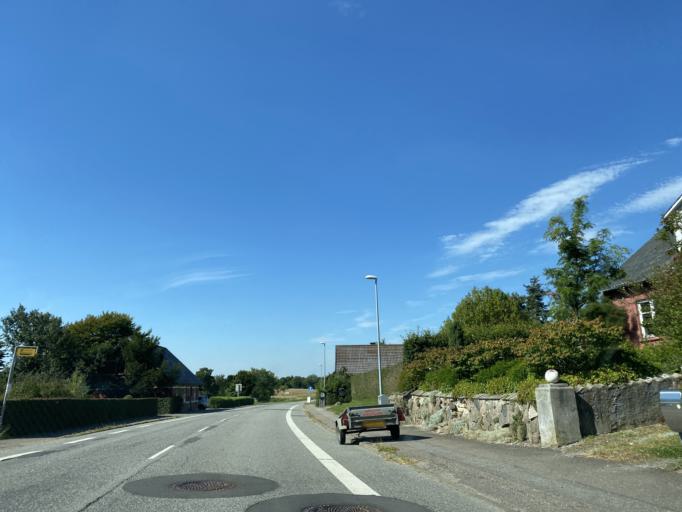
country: DK
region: Central Jutland
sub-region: Hedensted Kommune
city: Torring
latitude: 55.8014
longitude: 9.4629
